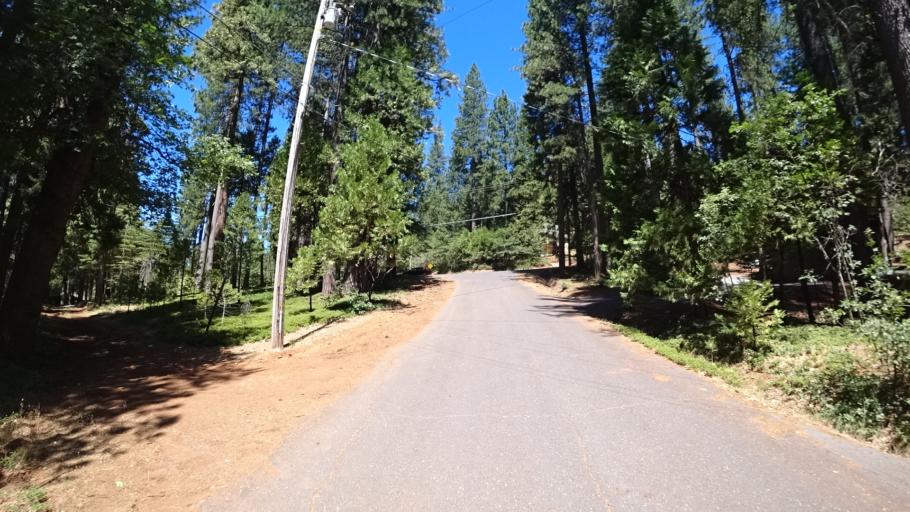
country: US
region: California
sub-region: Calaveras County
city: Arnold
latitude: 38.2362
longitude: -120.3355
